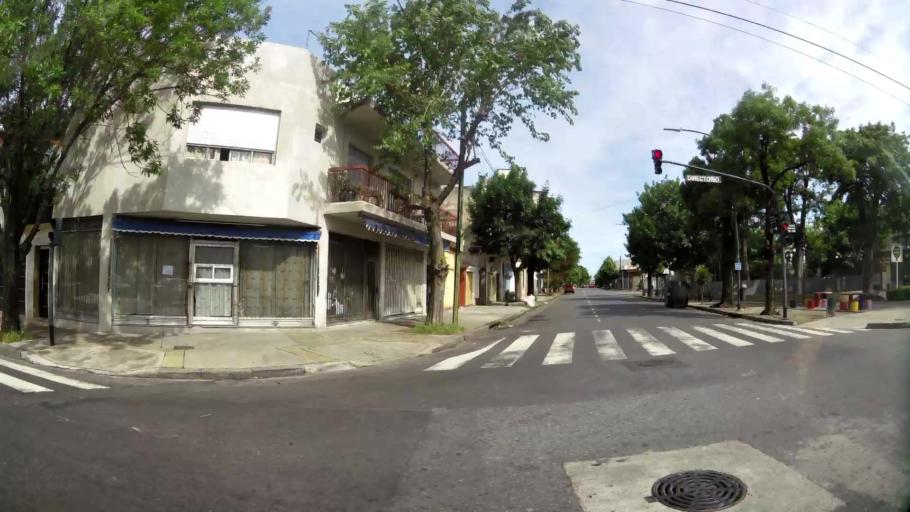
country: AR
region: Buenos Aires F.D.
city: Villa Lugano
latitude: -34.6619
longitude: -58.5052
